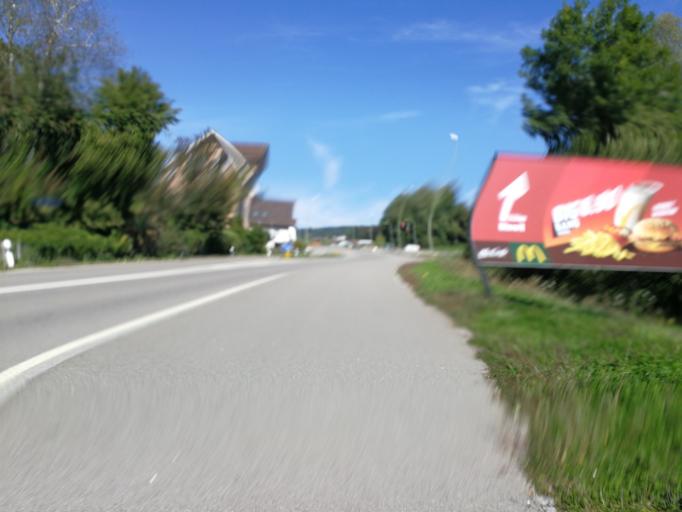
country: CH
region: Zurich
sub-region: Bezirk Hinwil
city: Hinwil
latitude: 47.2878
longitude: 8.8442
